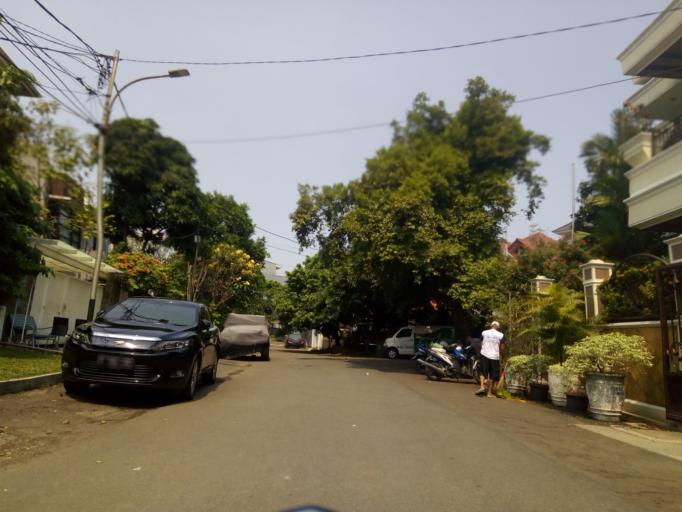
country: ID
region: Jakarta Raya
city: Jakarta
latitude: -6.2380
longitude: 106.7913
